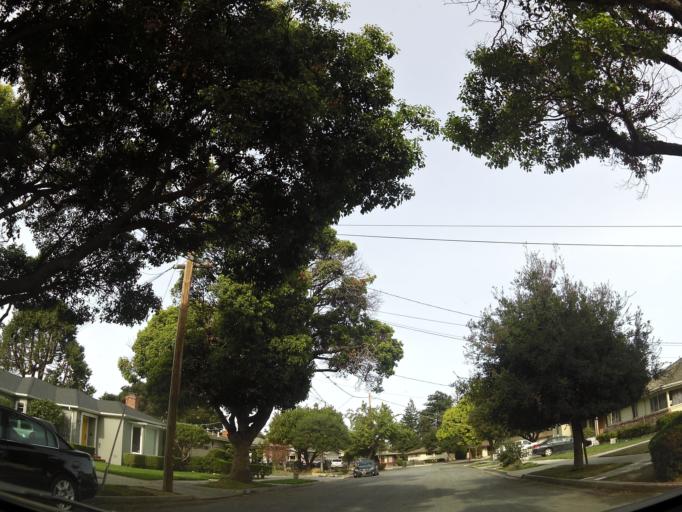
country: US
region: California
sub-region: Monterey County
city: Salinas
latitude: 36.6742
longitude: -121.6625
